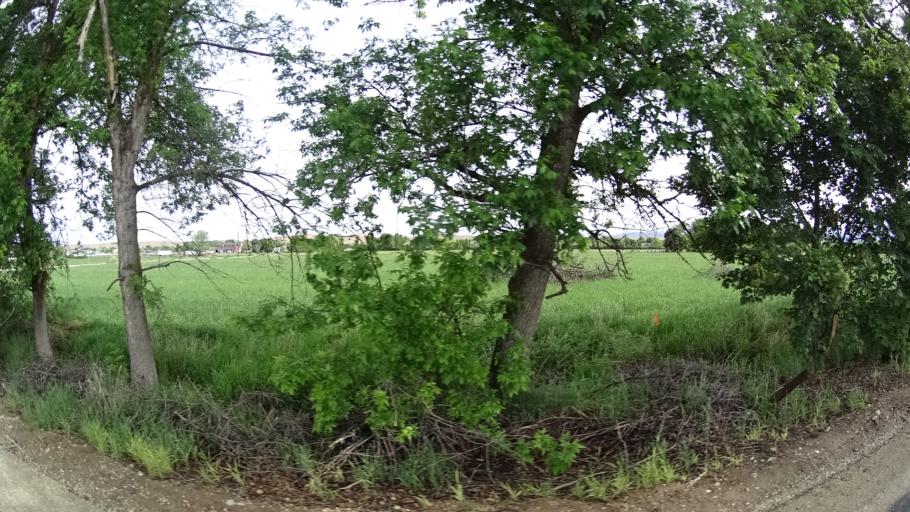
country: US
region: Idaho
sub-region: Ada County
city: Eagle
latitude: 43.7209
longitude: -116.4024
